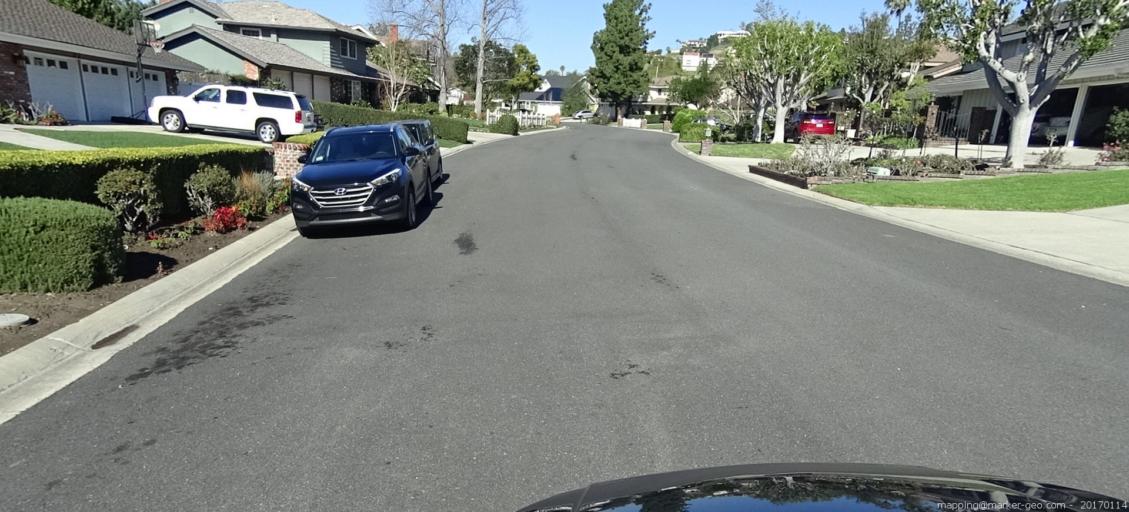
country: US
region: California
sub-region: Orange County
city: North Tustin
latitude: 33.7713
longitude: -117.8003
